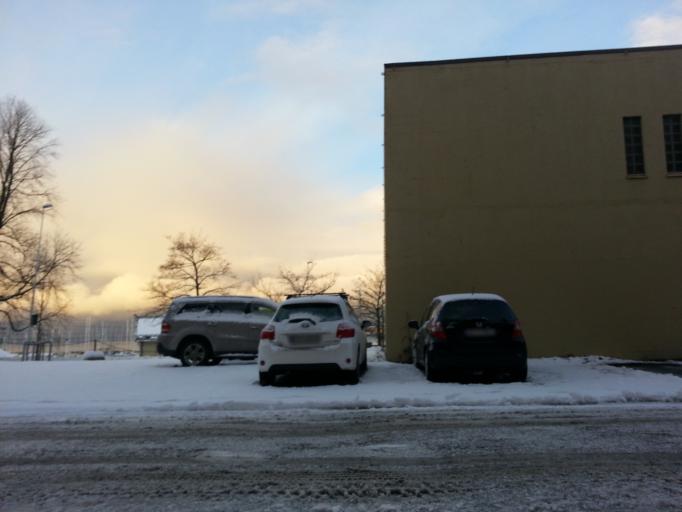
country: NO
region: Sor-Trondelag
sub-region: Trondheim
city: Trondheim
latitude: 63.4305
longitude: 10.3783
